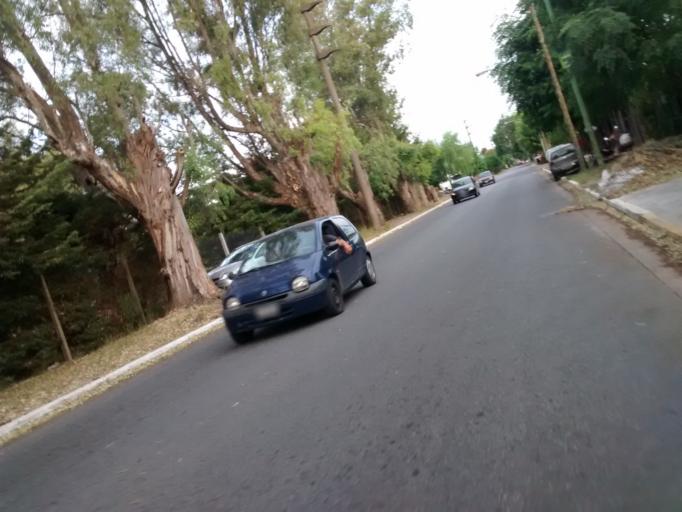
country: AR
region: Buenos Aires
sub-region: Partido de La Plata
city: La Plata
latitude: -34.8939
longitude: -58.0286
